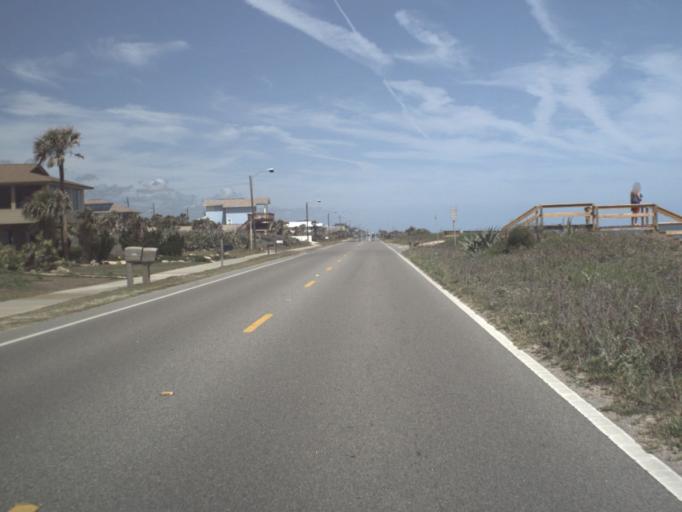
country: US
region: Florida
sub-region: Flagler County
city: Flagler Beach
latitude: 29.4471
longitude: -81.1116
